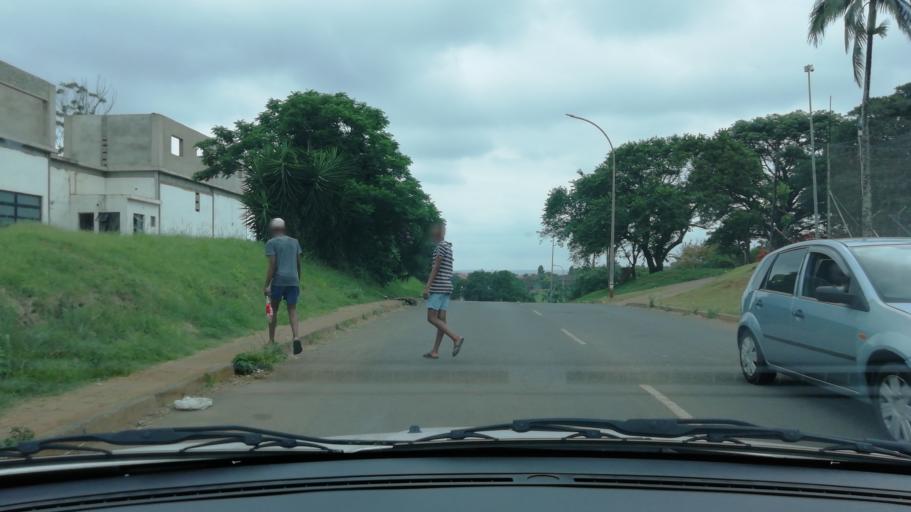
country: ZA
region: KwaZulu-Natal
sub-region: uThungulu District Municipality
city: Empangeni
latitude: -28.7462
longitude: 31.8879
